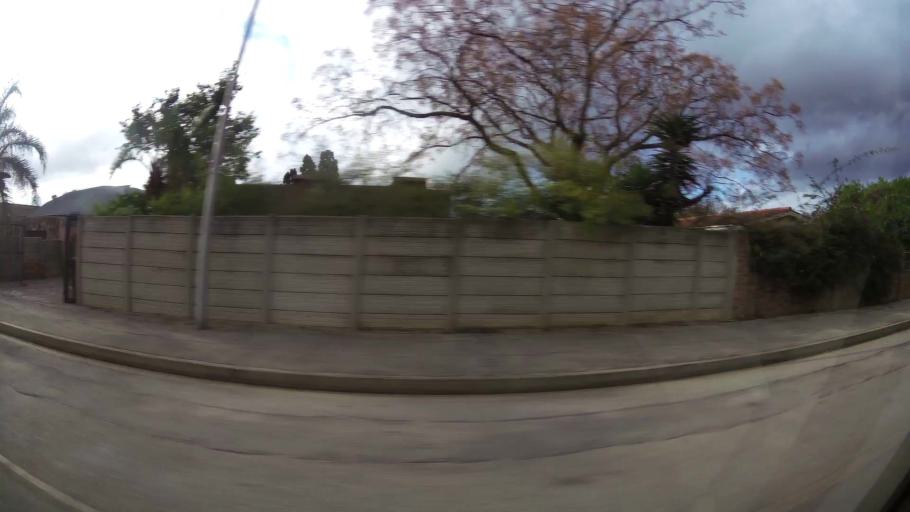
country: ZA
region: Eastern Cape
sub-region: Nelson Mandela Bay Metropolitan Municipality
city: Uitenhage
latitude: -33.8050
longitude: 25.4858
